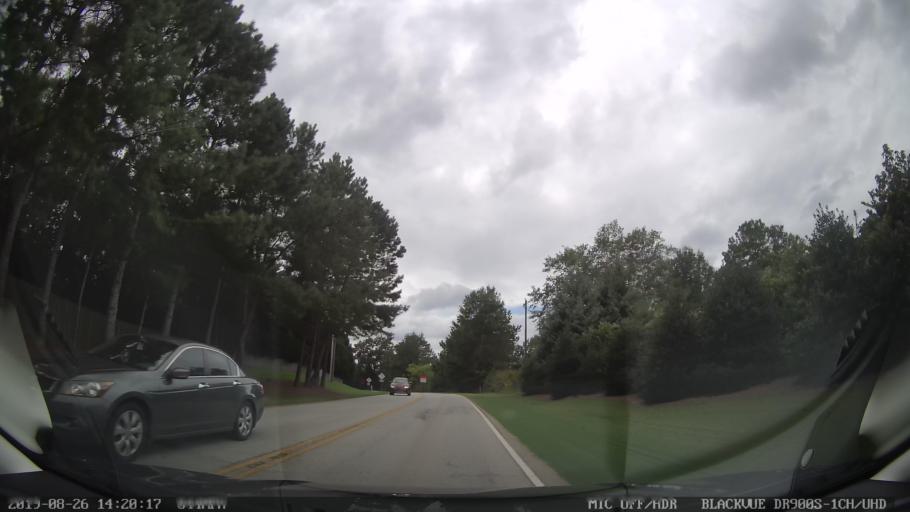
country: US
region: South Carolina
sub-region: Greenville County
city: Five Forks
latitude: 34.7997
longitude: -82.2498
